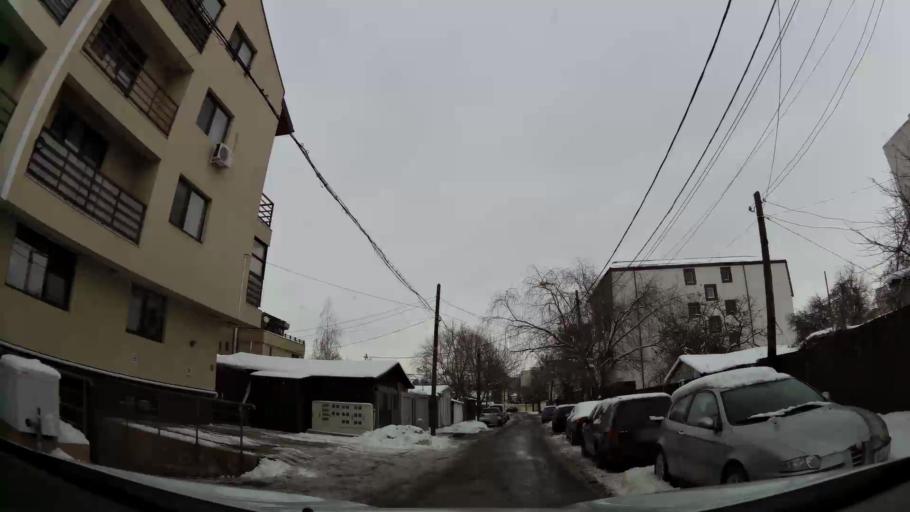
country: RO
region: Bucuresti
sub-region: Municipiul Bucuresti
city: Bucuresti
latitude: 44.3902
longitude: 26.1060
